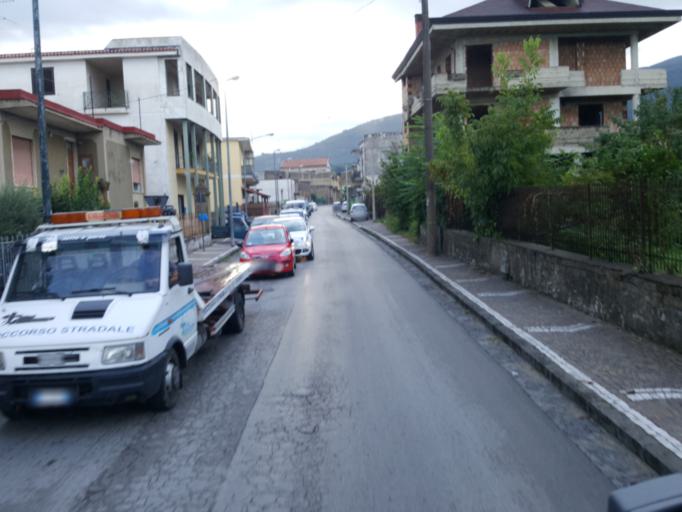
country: IT
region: Campania
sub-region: Provincia di Napoli
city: Palma Campania
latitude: 40.8799
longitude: 14.5512
